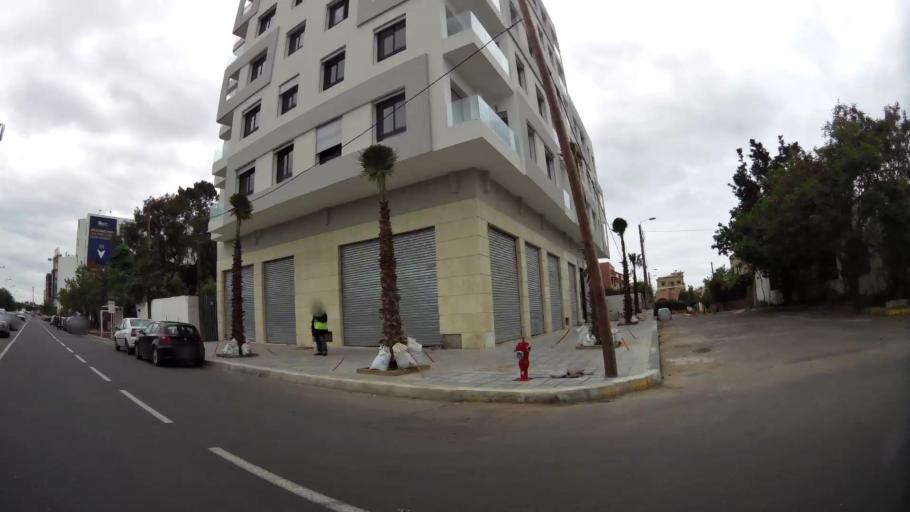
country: MA
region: Grand Casablanca
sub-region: Casablanca
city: Casablanca
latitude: 33.5592
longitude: -7.6298
